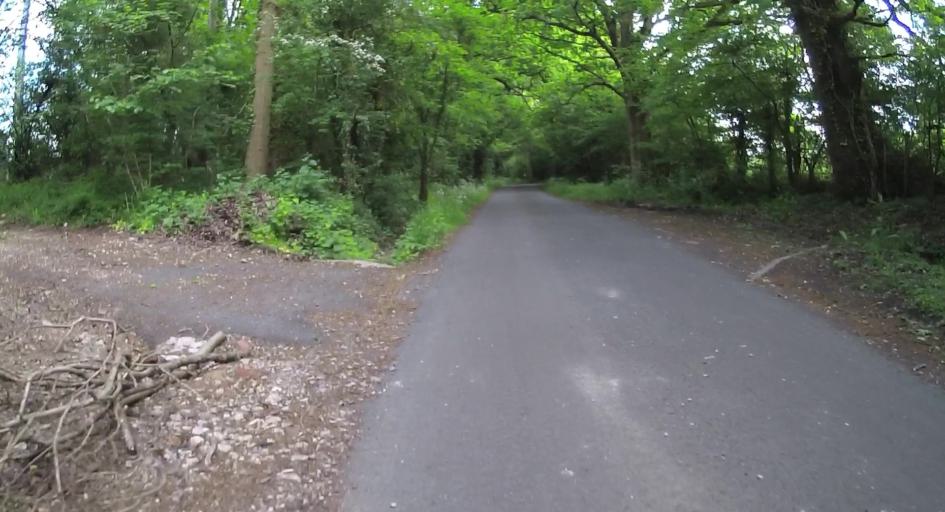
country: GB
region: England
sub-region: Hampshire
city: Fleet
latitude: 51.2360
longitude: -0.8535
